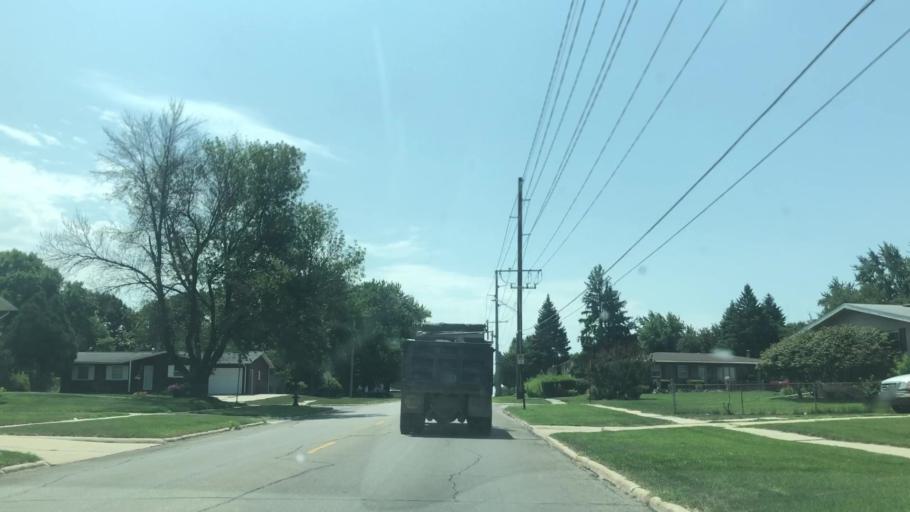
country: US
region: Iowa
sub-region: Marshall County
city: Marshalltown
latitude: 42.0196
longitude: -92.9221
